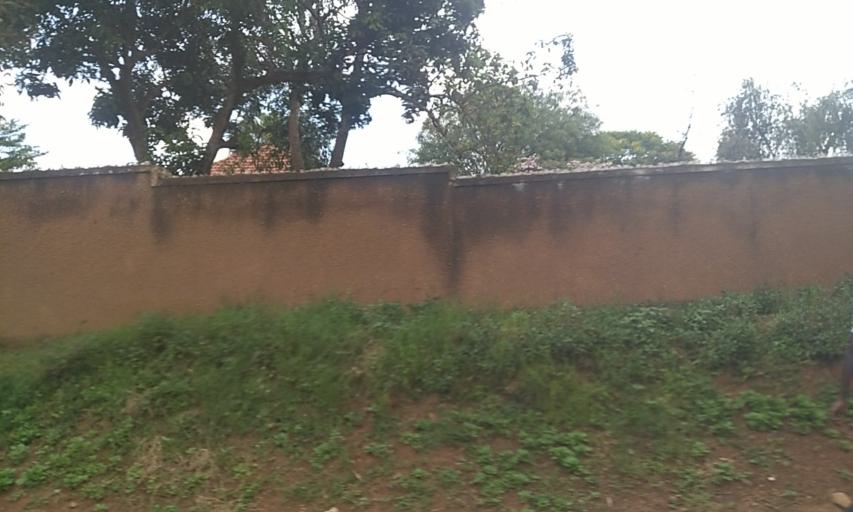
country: UG
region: Central Region
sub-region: Wakiso District
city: Kireka
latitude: 0.3431
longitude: 32.6254
